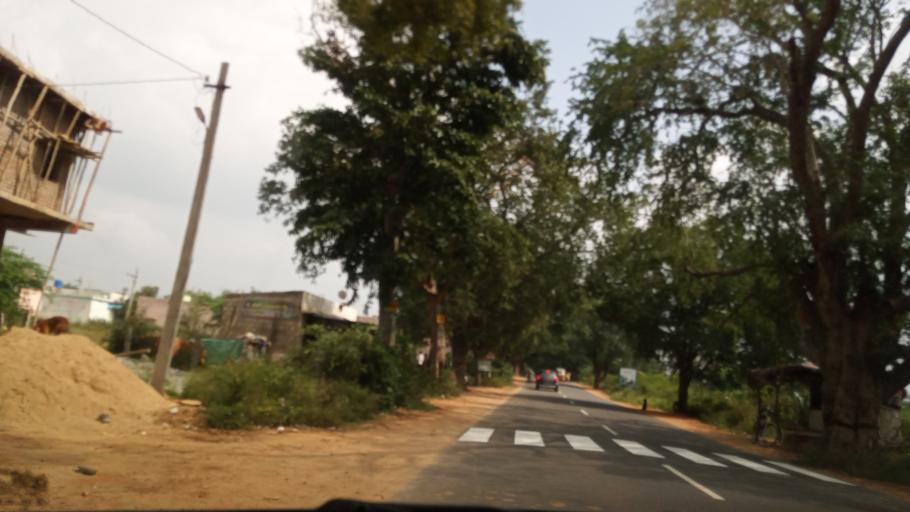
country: IN
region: Andhra Pradesh
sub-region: Chittoor
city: Madanapalle
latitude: 13.6361
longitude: 78.6406
